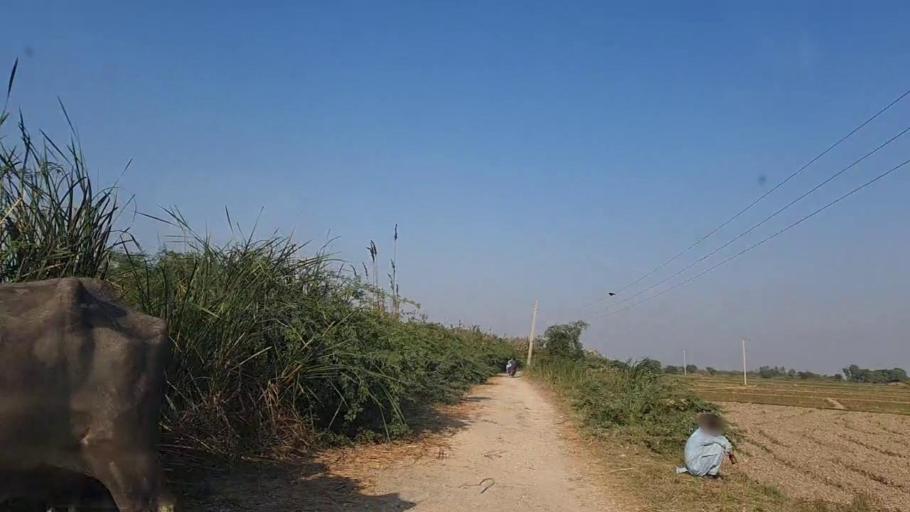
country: PK
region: Sindh
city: Thatta
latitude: 24.7195
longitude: 67.9436
